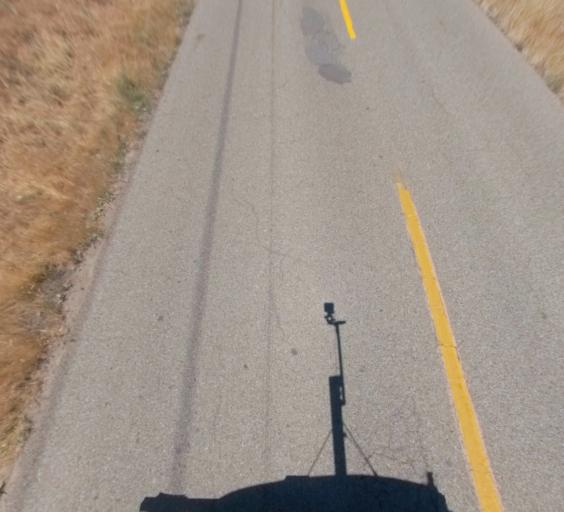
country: US
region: California
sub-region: Madera County
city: Bonadelle Ranchos-Madera Ranchos
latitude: 36.8947
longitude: -119.8185
